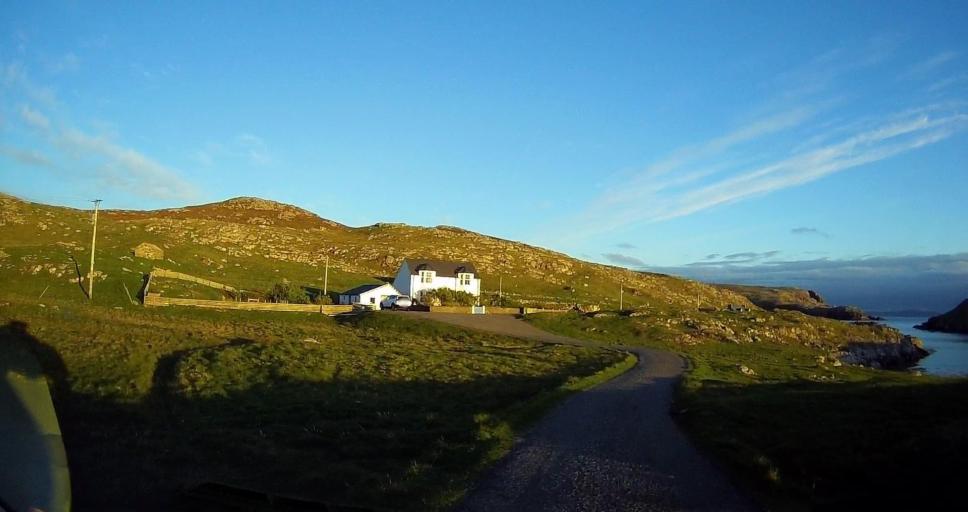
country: GB
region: Scotland
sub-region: Shetland Islands
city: Lerwick
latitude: 60.4418
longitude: -1.4477
